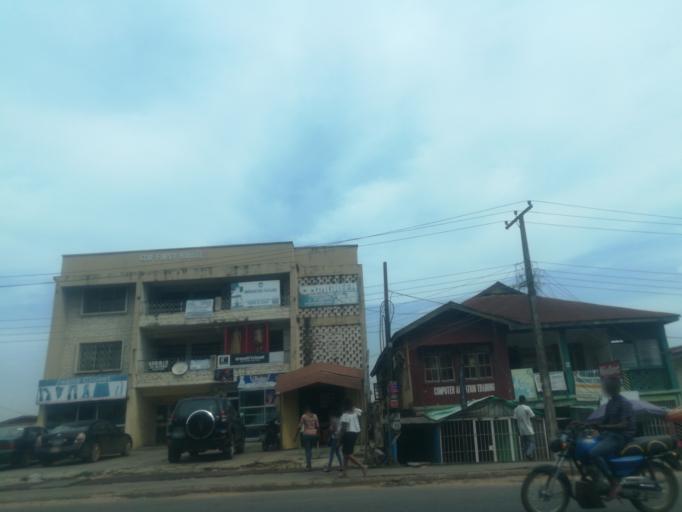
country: NG
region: Oyo
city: Ibadan
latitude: 7.4187
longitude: 3.8964
